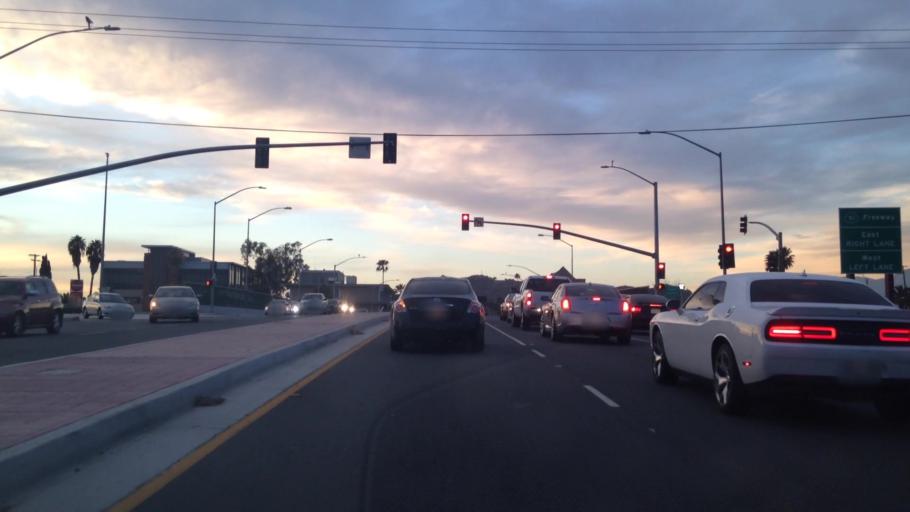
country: US
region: California
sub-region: Riverside County
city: Riverside
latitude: 33.9732
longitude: -117.3721
